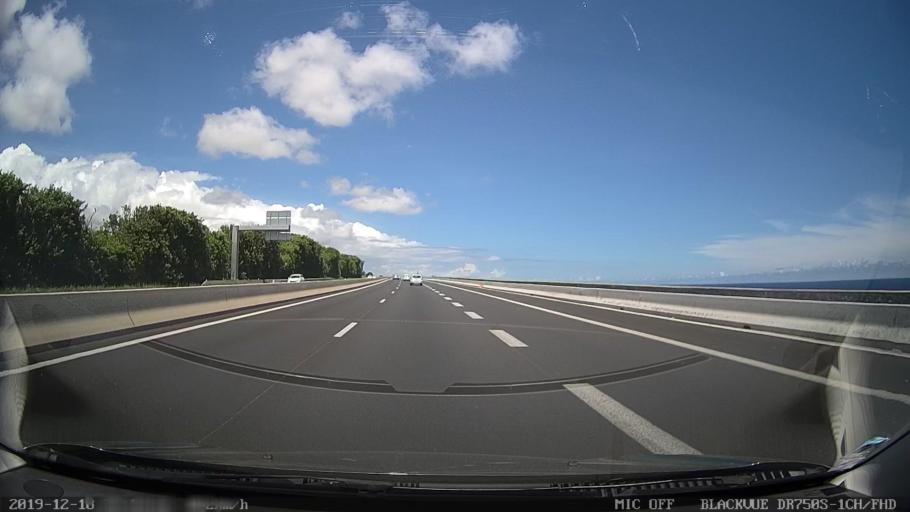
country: RE
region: Reunion
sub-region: Reunion
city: Sainte-Suzanne
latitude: -20.9014
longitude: 55.5939
